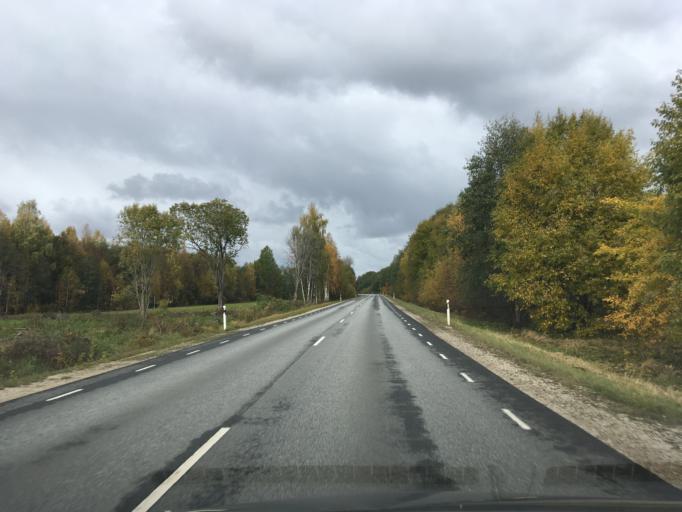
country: EE
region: Harju
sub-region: Anija vald
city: Kehra
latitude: 59.3015
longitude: 25.3599
